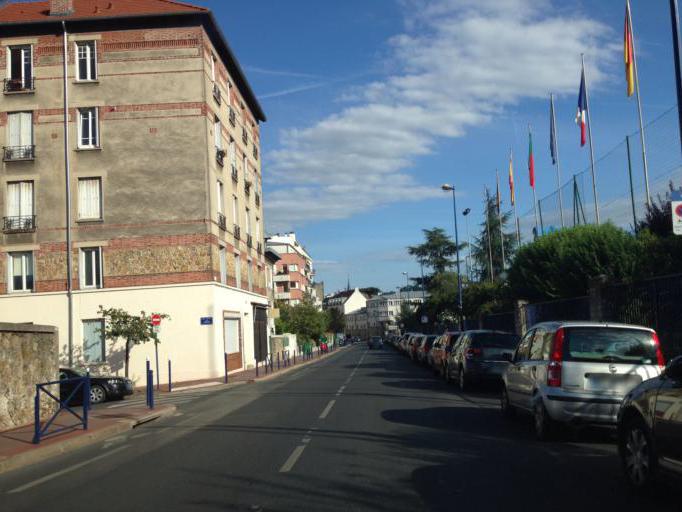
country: FR
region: Ile-de-France
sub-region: Departement des Hauts-de-Seine
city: Clamart
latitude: 48.8015
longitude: 2.2597
